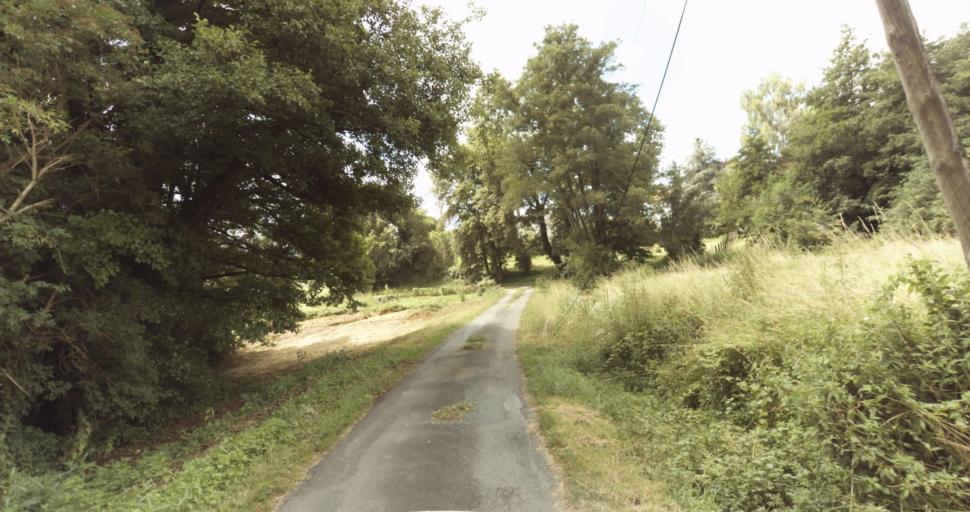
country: FR
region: Aquitaine
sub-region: Departement de la Gironde
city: Bazas
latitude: 44.4381
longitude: -0.2175
